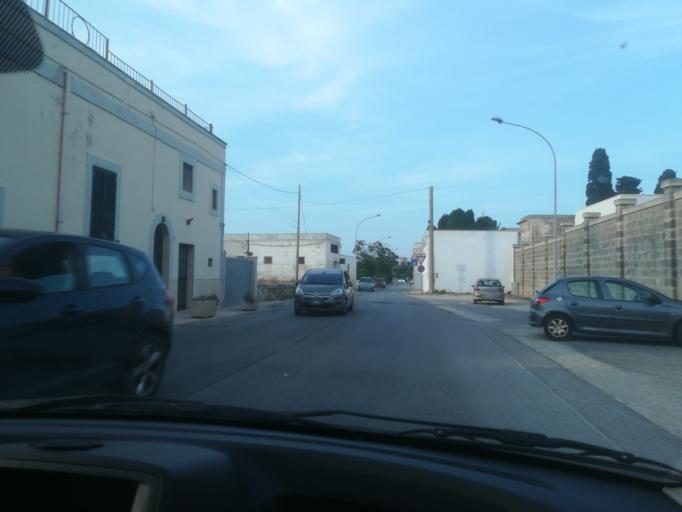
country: IT
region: Apulia
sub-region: Provincia di Bari
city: Monopoli
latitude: 40.9425
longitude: 17.2978
